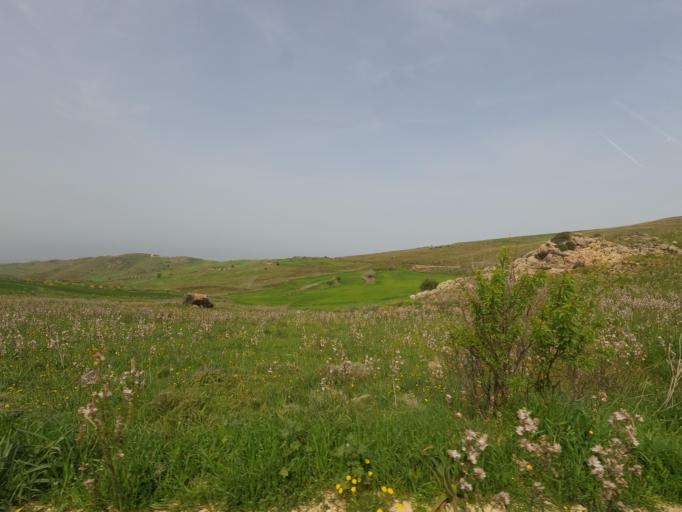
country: CY
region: Pafos
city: Polis
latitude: 34.9754
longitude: 32.3601
